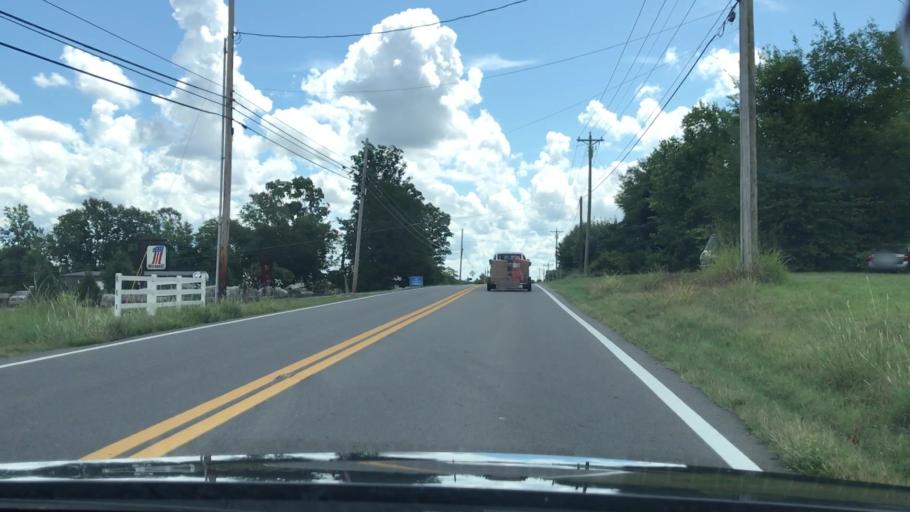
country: US
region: Tennessee
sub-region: Rutherford County
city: Smyrna
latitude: 35.8452
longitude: -86.5518
